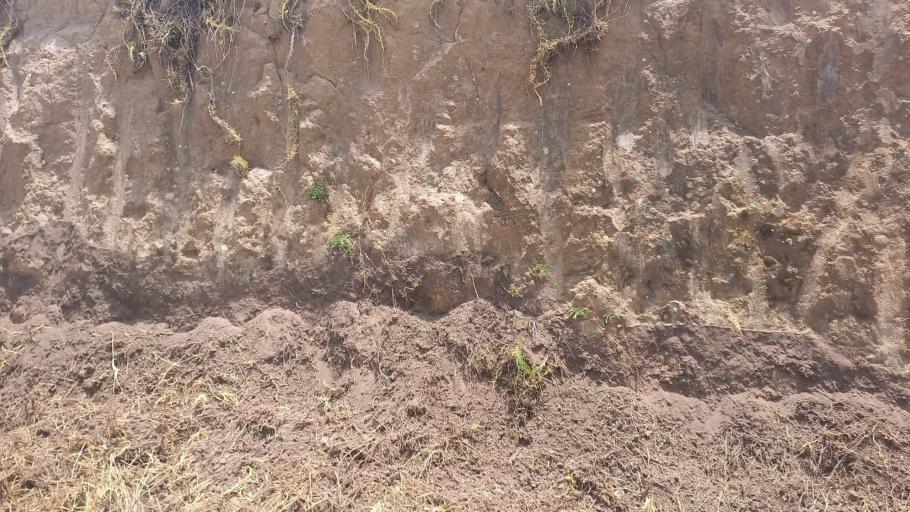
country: EC
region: Pichincha
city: Cayambe
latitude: 0.1732
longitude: -78.0893
